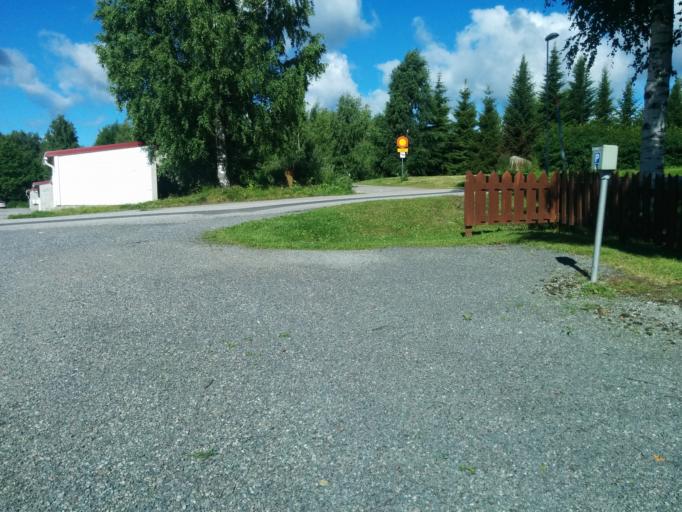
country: FI
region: Pirkanmaa
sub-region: Tampere
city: Orivesi
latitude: 61.6729
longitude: 24.3629
